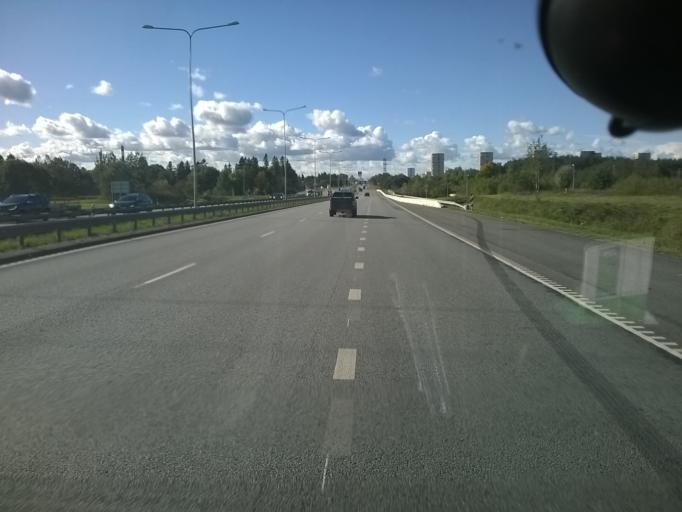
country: EE
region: Harju
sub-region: Joelaehtme vald
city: Loo
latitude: 59.4456
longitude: 24.9197
